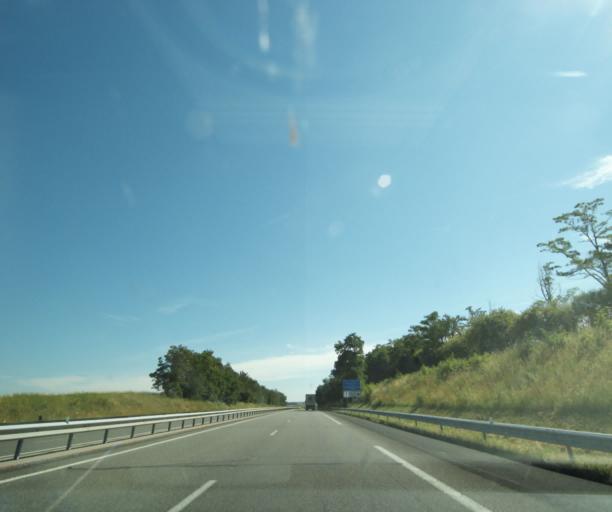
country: FR
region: Lorraine
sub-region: Departement des Vosges
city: Bulgneville
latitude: 48.1988
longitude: 5.7889
